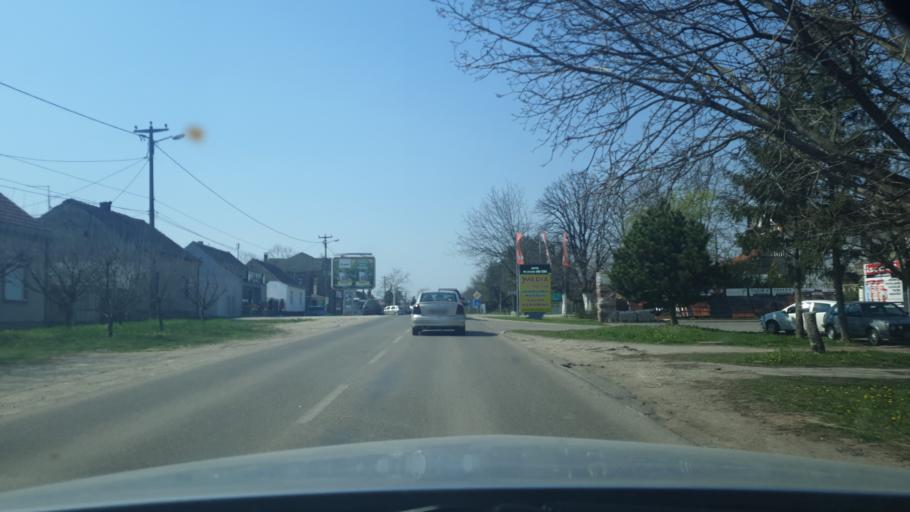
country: RS
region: Autonomna Pokrajina Vojvodina
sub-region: Sremski Okrug
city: Ruma
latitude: 45.0082
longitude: 19.7989
